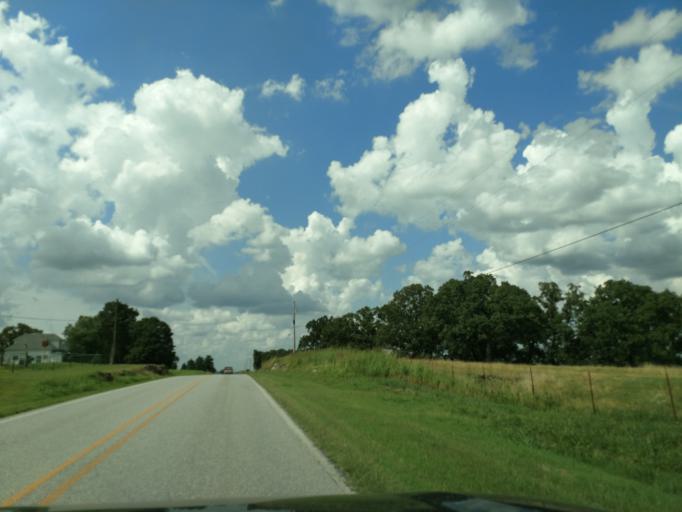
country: US
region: Arkansas
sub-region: Carroll County
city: Berryville
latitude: 36.4451
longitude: -93.5561
